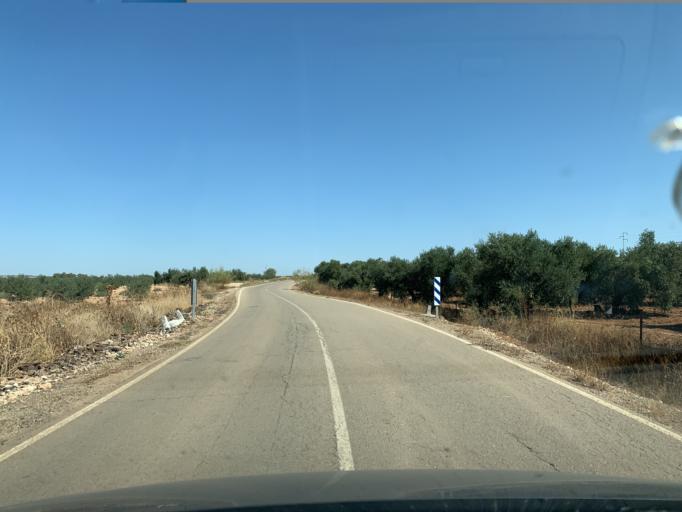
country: ES
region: Andalusia
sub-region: Provincia de Sevilla
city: La Lantejuela
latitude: 37.3402
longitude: -5.2746
